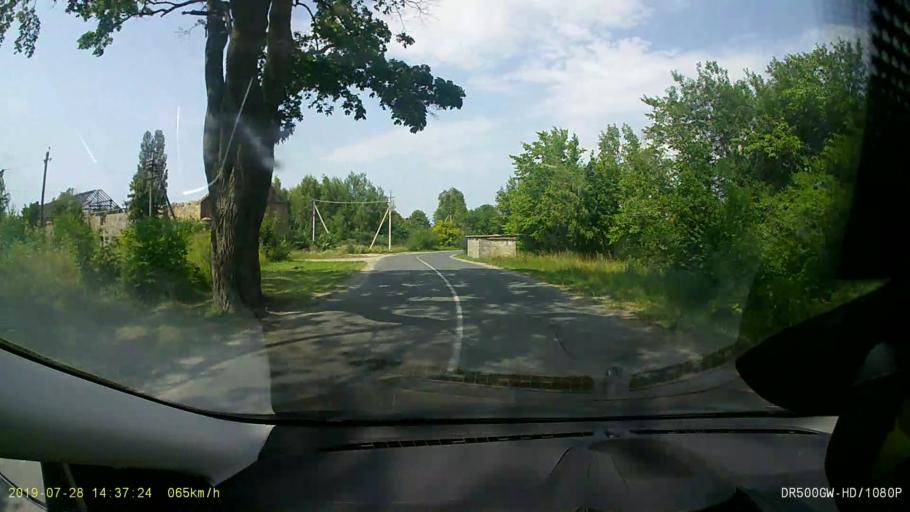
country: RU
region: Kaliningrad
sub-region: Gorod Kaliningrad
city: Yantarnyy
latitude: 54.8687
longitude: 19.9419
